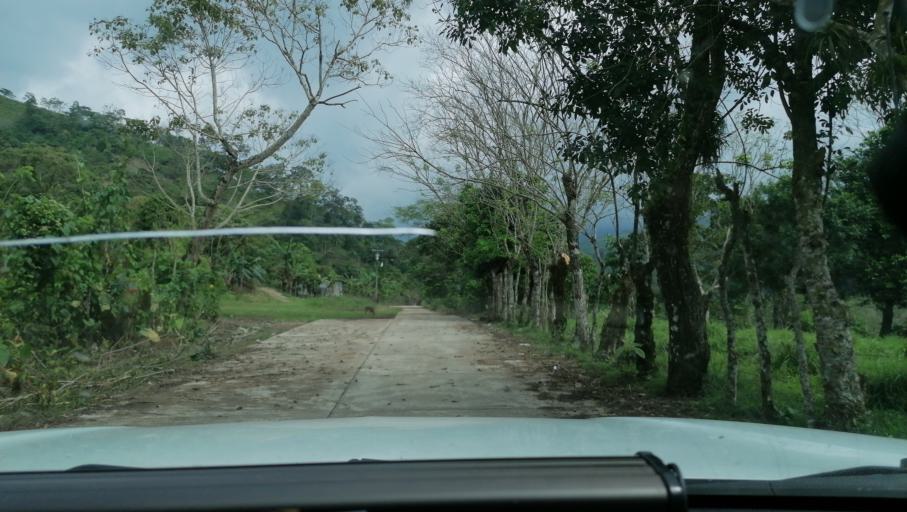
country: MX
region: Chiapas
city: Ocotepec
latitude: 17.3250
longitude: -93.1672
